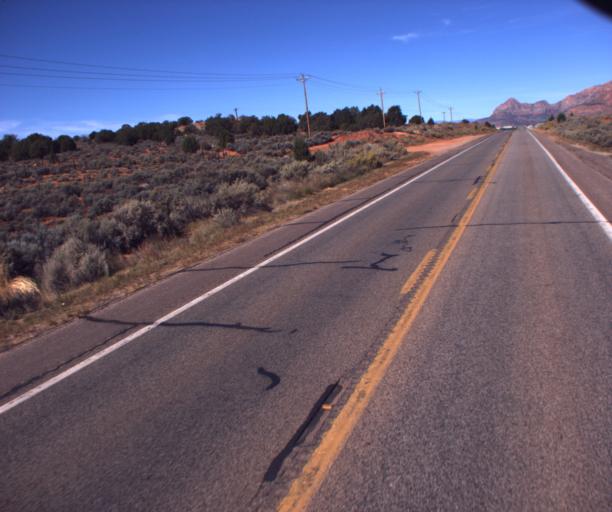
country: US
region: Arizona
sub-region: Mohave County
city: Colorado City
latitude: 36.9666
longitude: -112.9718
